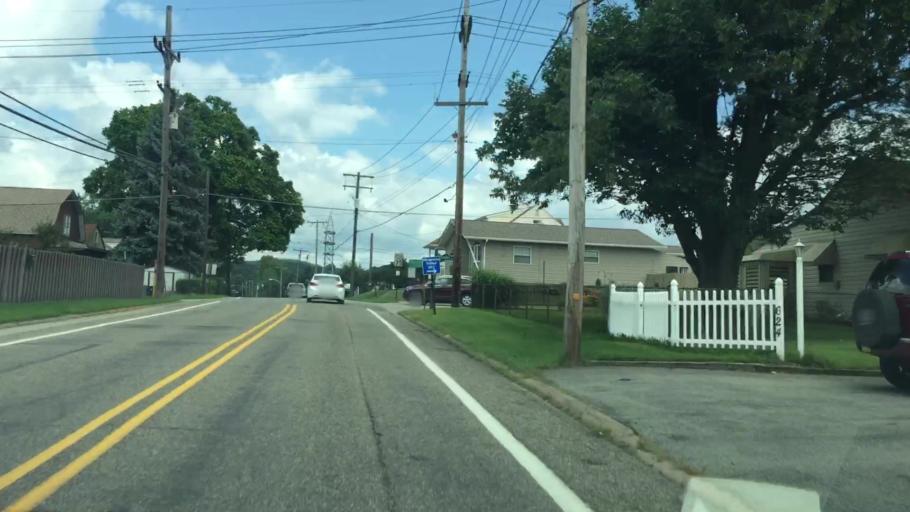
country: US
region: Pennsylvania
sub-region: Allegheny County
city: Cheswick
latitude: 40.5486
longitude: -79.8046
